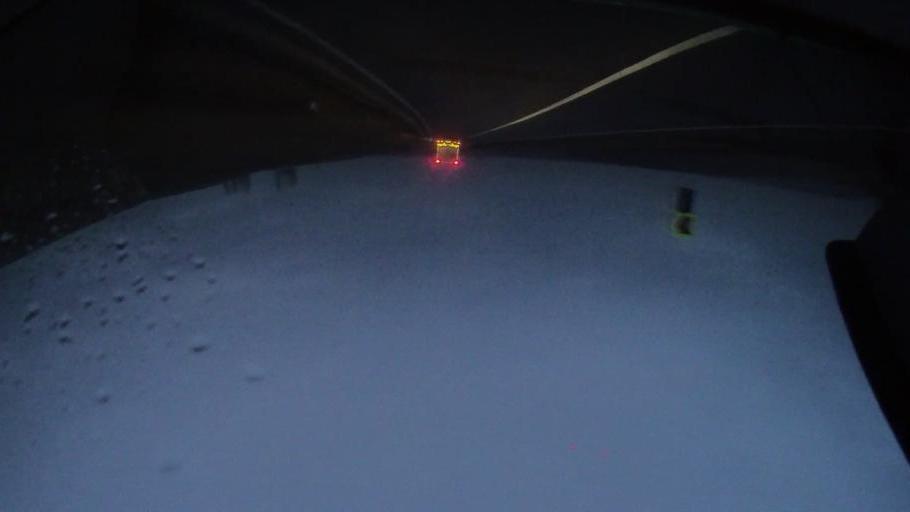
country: RO
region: Harghita
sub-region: Comuna Subcetate
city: Subcetate
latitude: 46.8467
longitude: 25.4694
